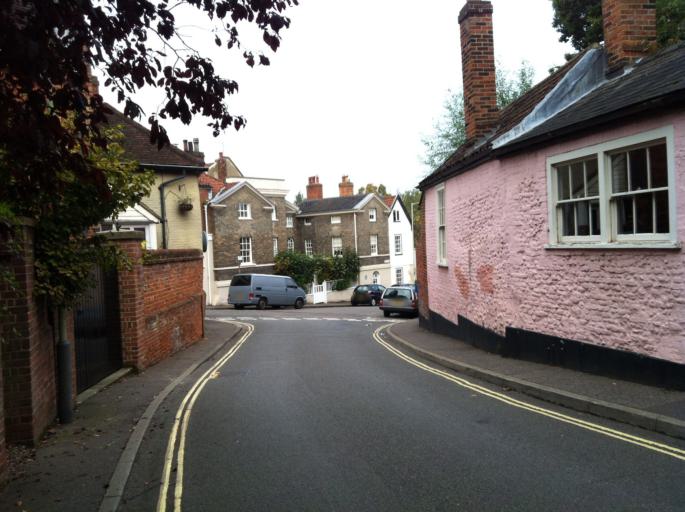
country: GB
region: England
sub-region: Norfolk
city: Norwich
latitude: 52.6300
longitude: 1.2874
